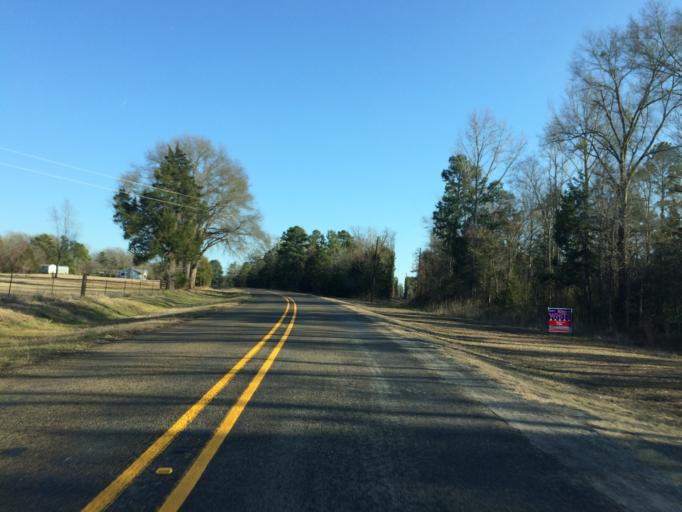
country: US
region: Texas
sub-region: Wood County
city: Mineola
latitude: 32.6901
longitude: -95.3449
